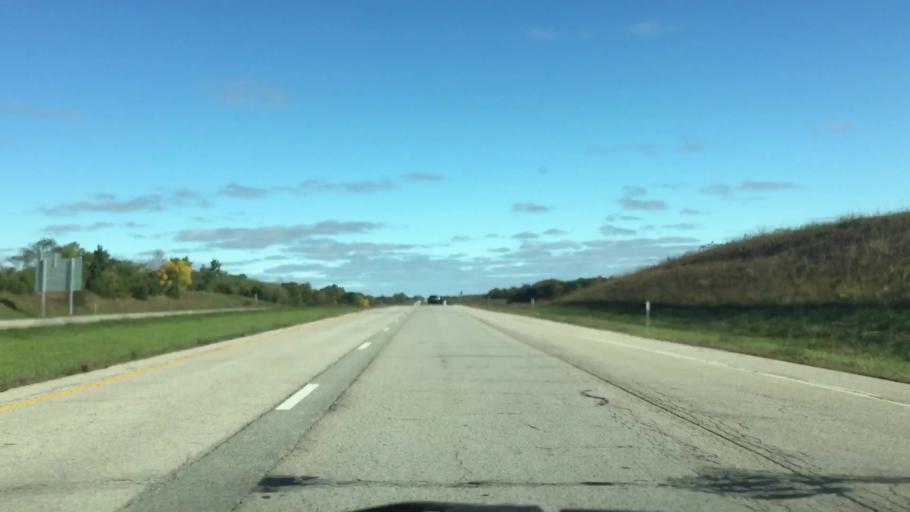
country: US
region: Missouri
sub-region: Harrison County
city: Bethany
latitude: 40.3785
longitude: -94.0016
